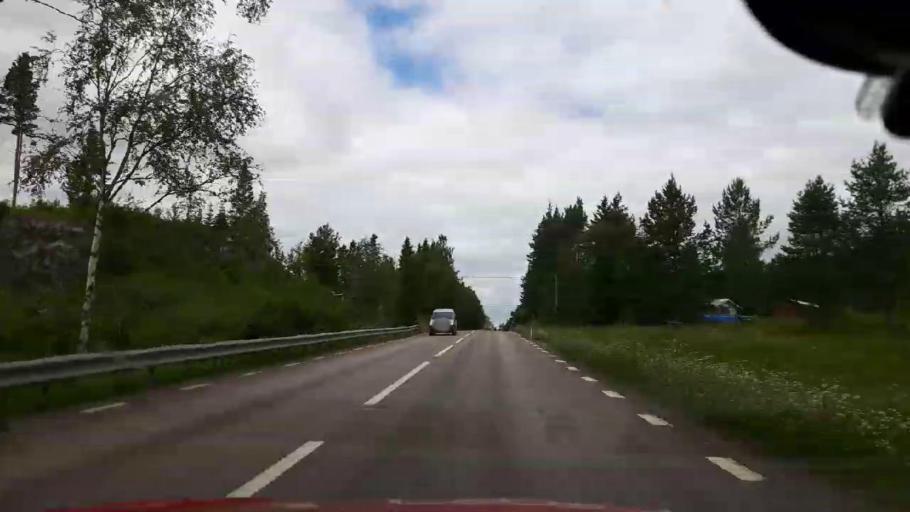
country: SE
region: Jaemtland
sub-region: OEstersunds Kommun
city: Brunflo
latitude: 63.0117
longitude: 14.9530
